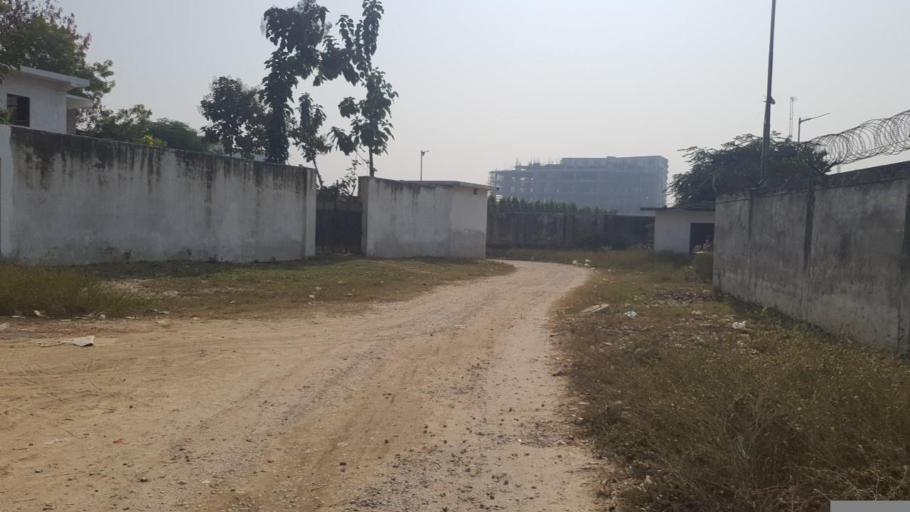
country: IN
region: Uttar Pradesh
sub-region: Lucknow District
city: Lucknow
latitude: 26.7997
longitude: 81.0047
